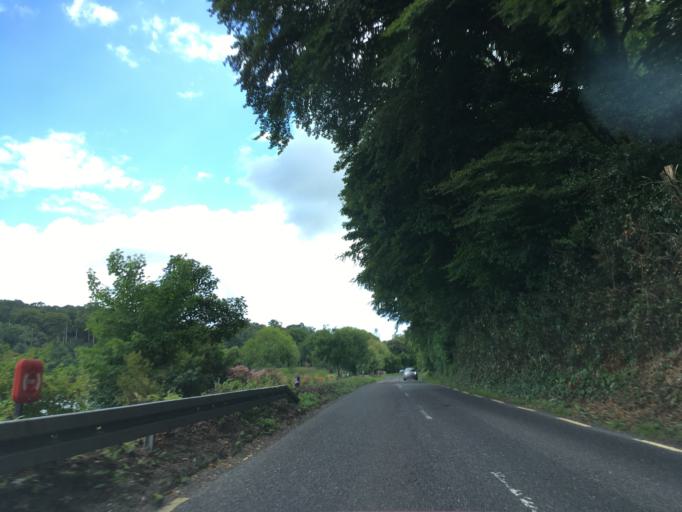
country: IE
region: Munster
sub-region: County Cork
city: Crosshaven
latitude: 51.8040
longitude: -8.3368
